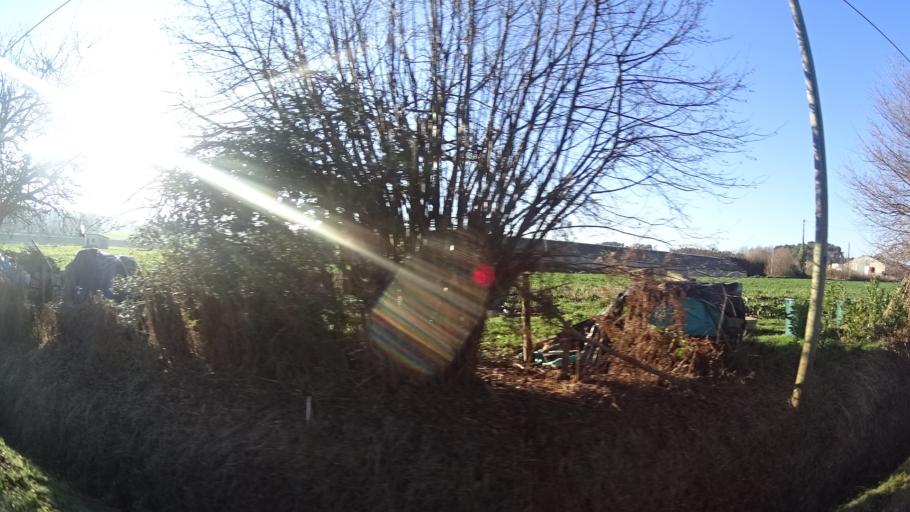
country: FR
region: Brittany
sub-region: Departement du Morbihan
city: Saint-Vincent-sur-Oust
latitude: 47.6753
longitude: -2.1749
